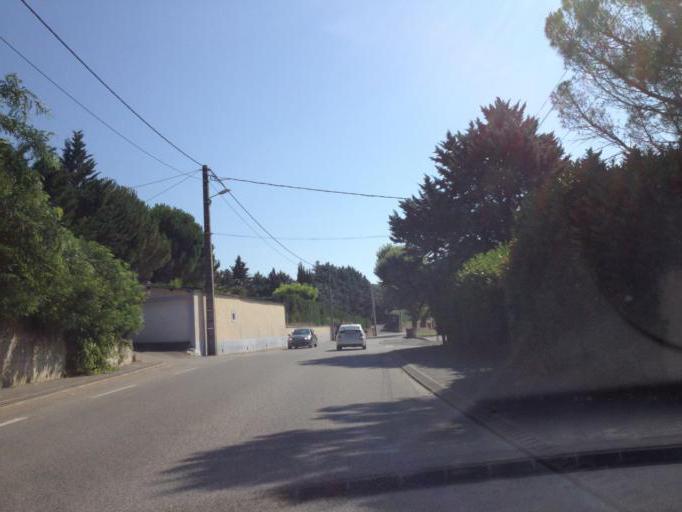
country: FR
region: Rhone-Alpes
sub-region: Departement de la Drome
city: Clerieux
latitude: 45.1203
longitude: 4.9728
